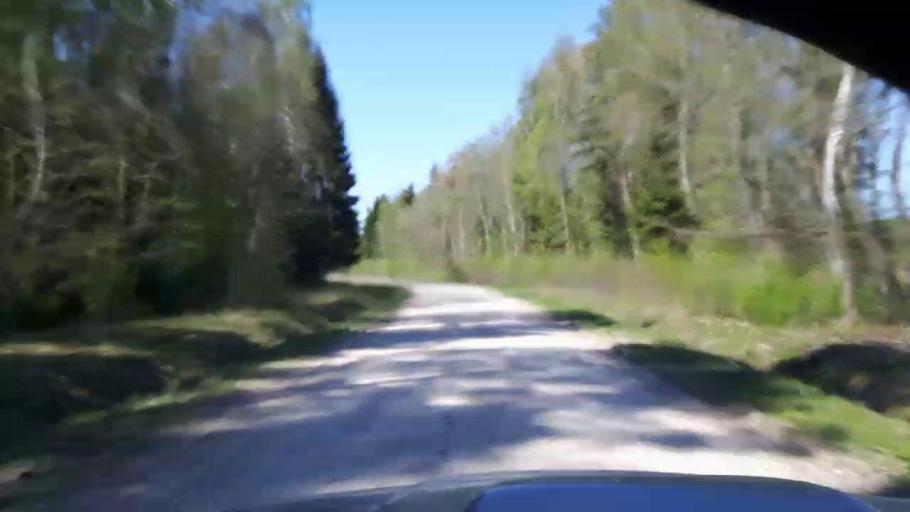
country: EE
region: Paernumaa
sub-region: Tootsi vald
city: Tootsi
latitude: 58.4735
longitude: 24.7577
